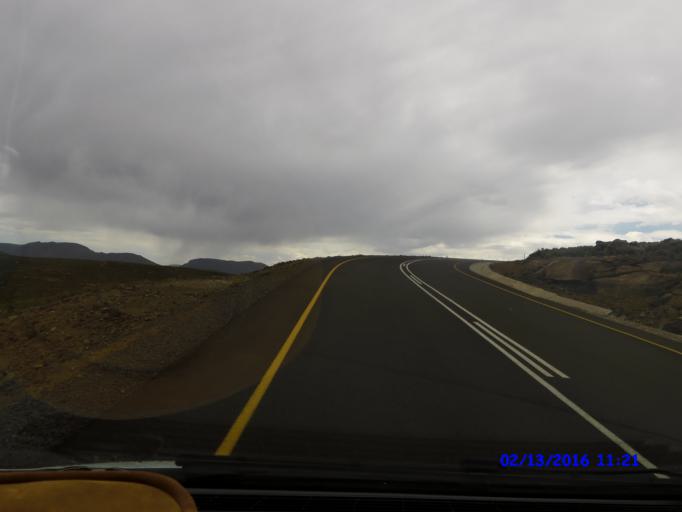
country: LS
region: Maseru
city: Nako
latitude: -29.7537
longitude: 27.9760
